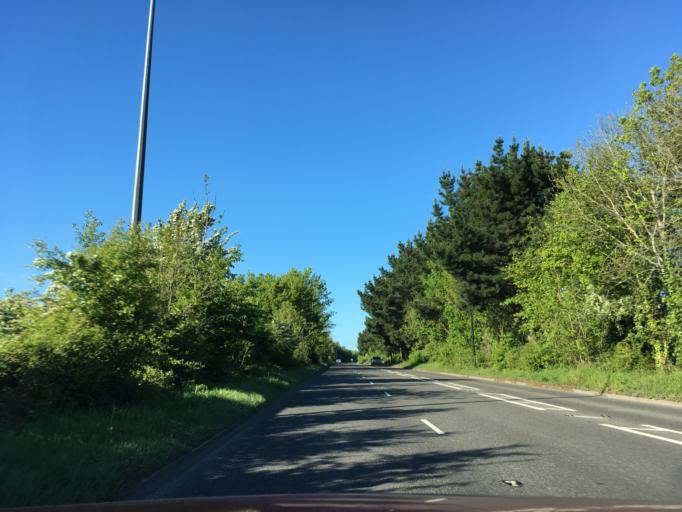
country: GB
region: England
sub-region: North Somerset
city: Long Ashton
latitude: 51.4259
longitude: -2.6517
